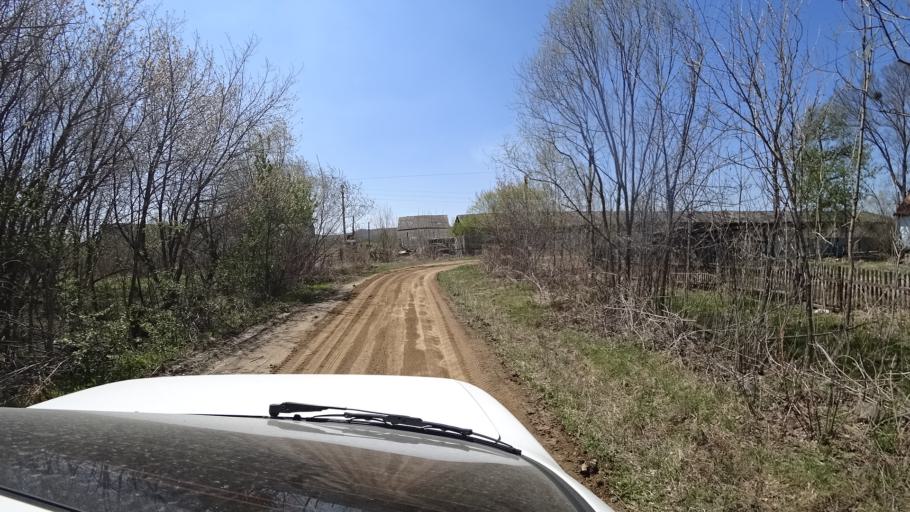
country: RU
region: Primorskiy
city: Lazo
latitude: 45.7981
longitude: 133.7618
